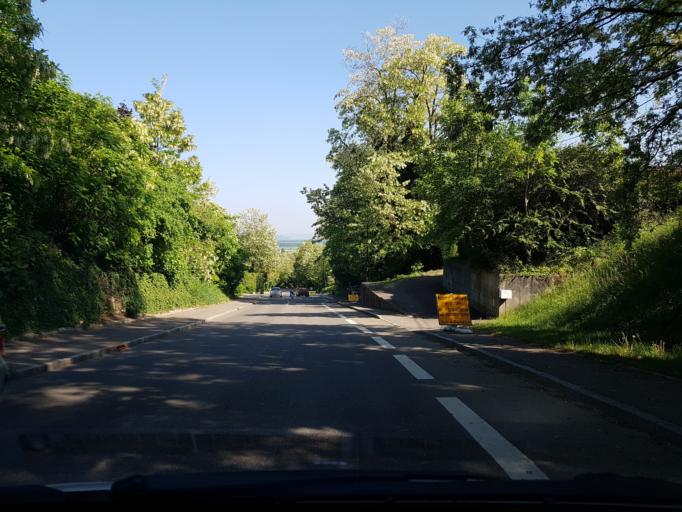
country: FR
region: Alsace
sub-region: Departement du Haut-Rhin
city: Zimmersheim
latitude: 47.7234
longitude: 7.3834
